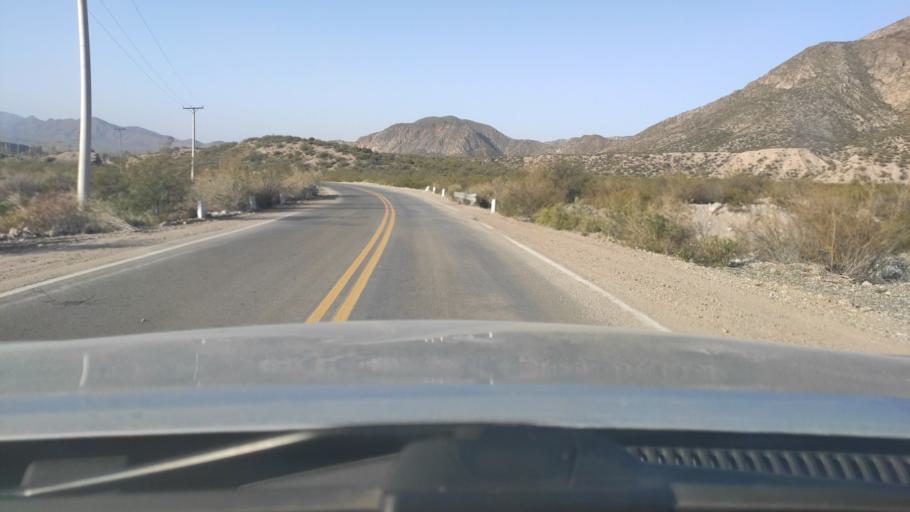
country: AR
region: San Juan
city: Villa Media Agua
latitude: -32.0081
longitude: -68.7703
